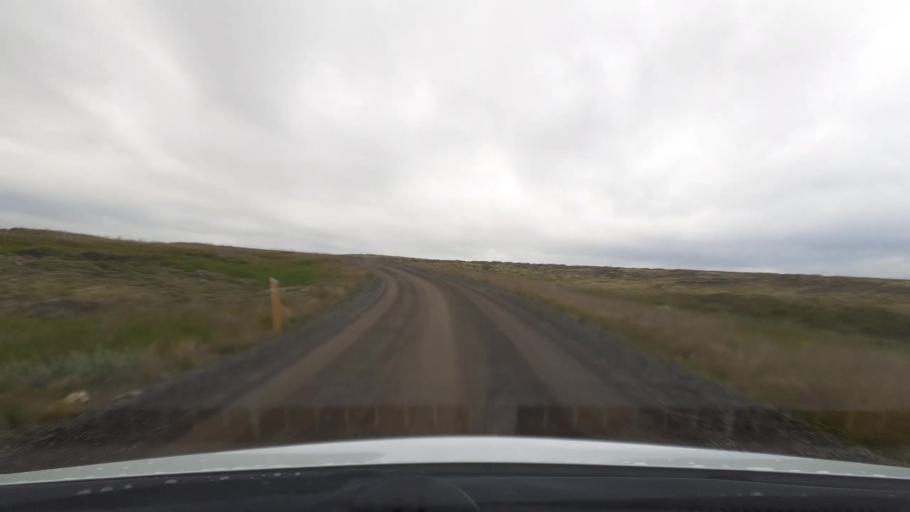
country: IS
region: Capital Region
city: Mosfellsbaer
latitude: 64.1979
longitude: -21.5561
